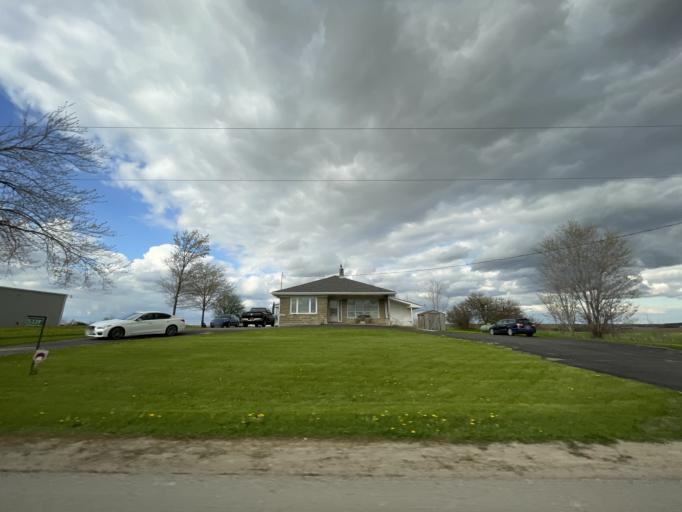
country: CA
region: Ontario
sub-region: Wellington County
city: Guelph
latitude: 43.5228
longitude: -80.3288
